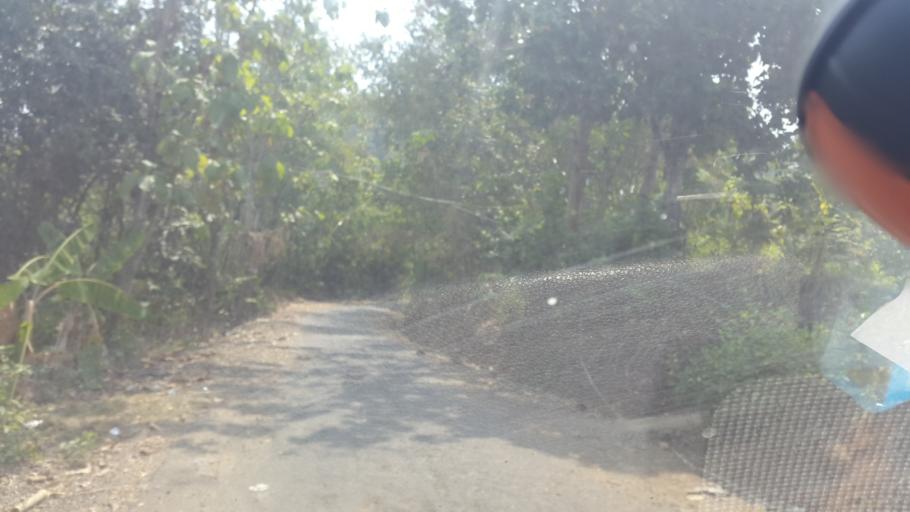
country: ID
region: West Java
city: Sindangsari
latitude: -6.9806
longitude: 106.6949
